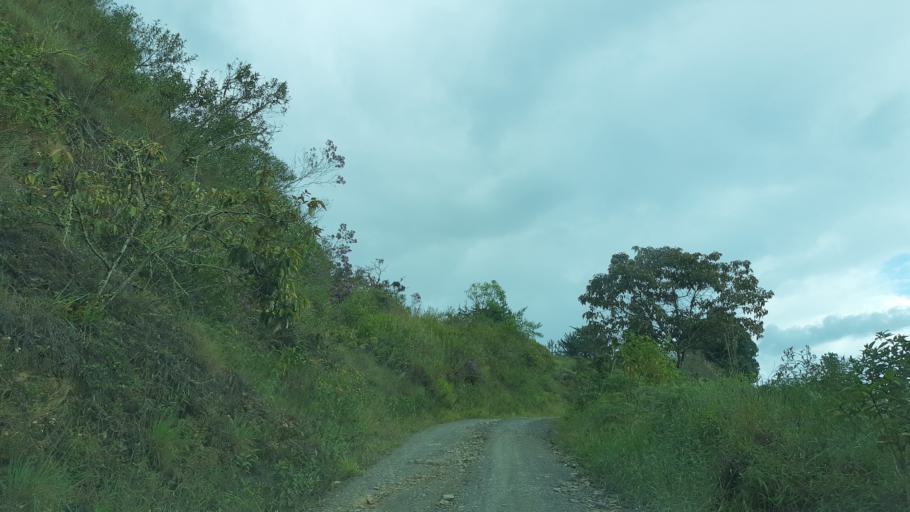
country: CO
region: Boyaca
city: Garagoa
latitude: 5.0042
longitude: -73.3390
